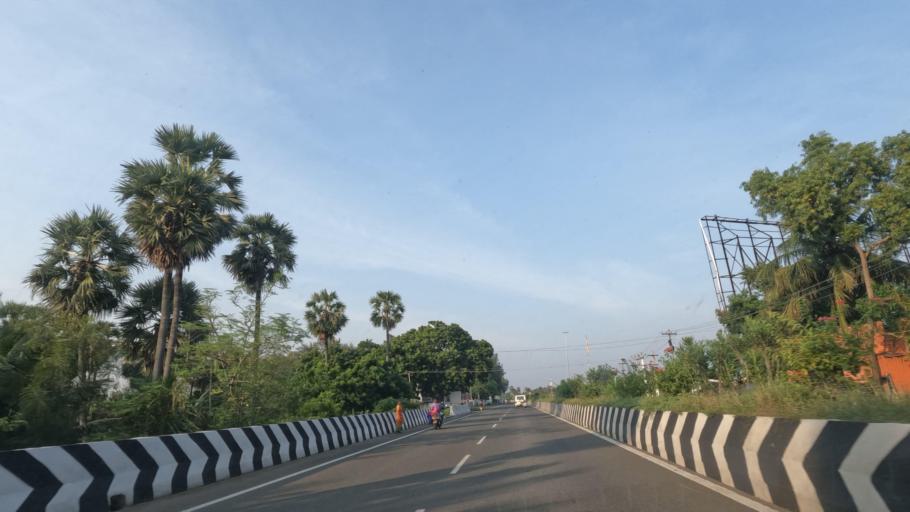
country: IN
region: Tamil Nadu
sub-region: Kancheepuram
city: Mamallapuram
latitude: 12.6523
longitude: 80.2052
